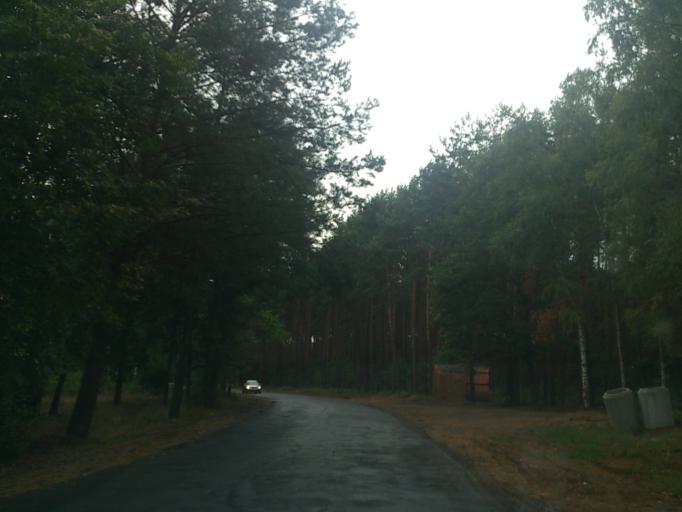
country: PL
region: Greater Poland Voivodeship
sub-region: Powiat gnieznienski
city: Kiszkowo
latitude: 52.5208
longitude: 17.1738
